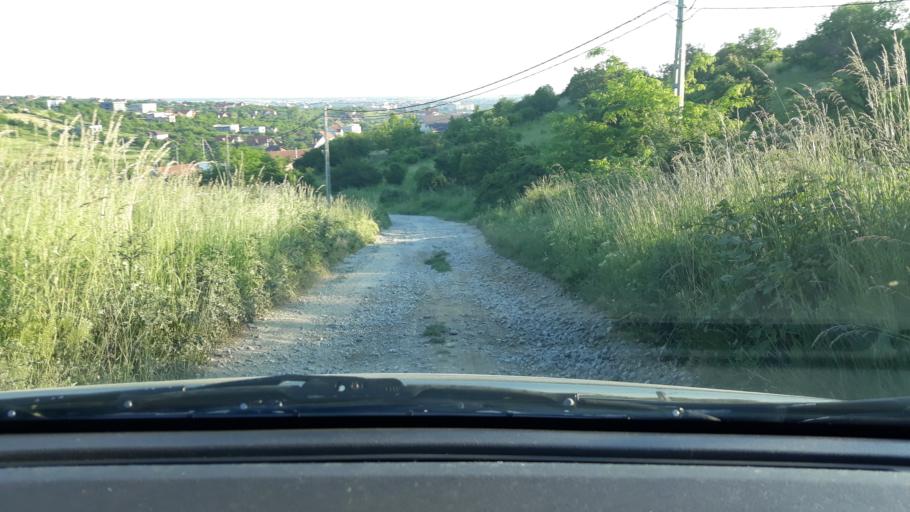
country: RO
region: Bihor
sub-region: Comuna Paleu
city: Paleu
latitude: 47.1009
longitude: 21.9350
